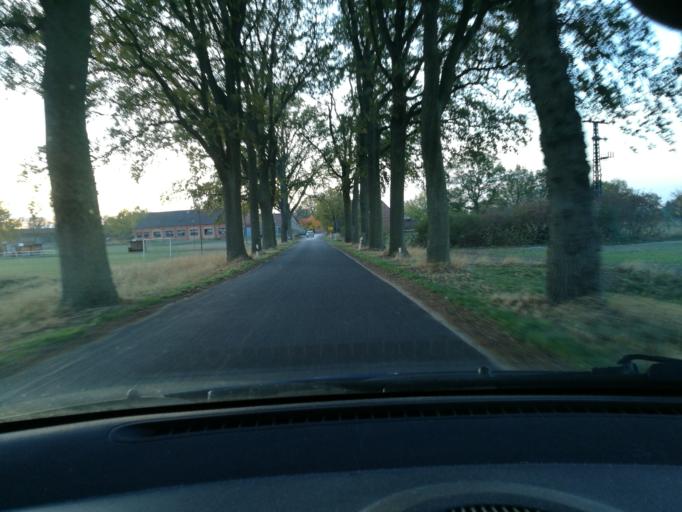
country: DE
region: Brandenburg
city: Karstadt
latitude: 53.0990
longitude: 11.7015
